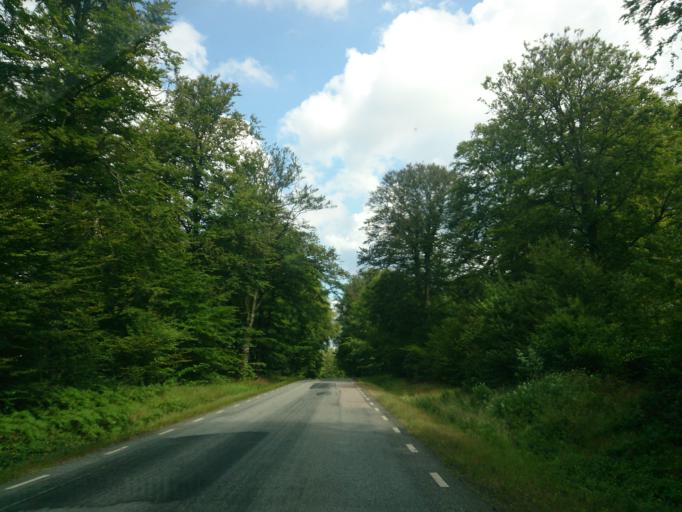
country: SE
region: Joenkoeping
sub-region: Varnamo Kommun
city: Forsheda
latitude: 57.1361
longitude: 13.8738
